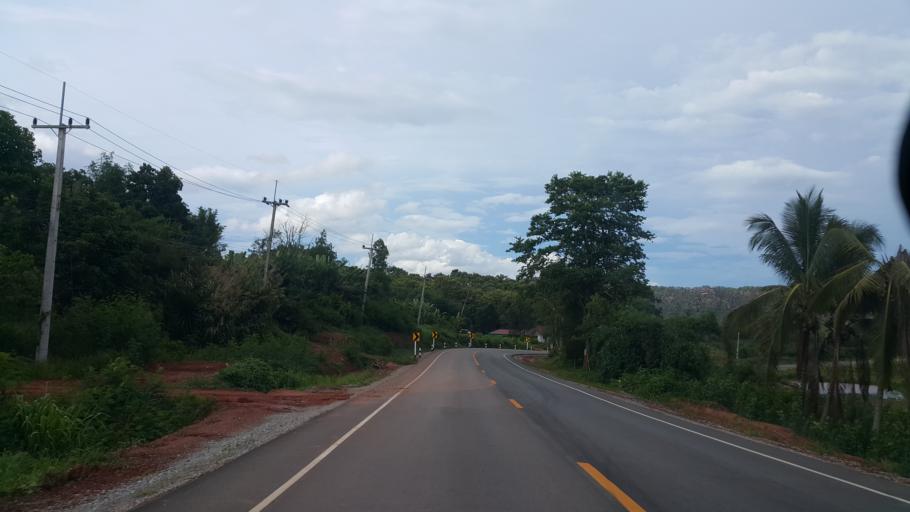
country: TH
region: Loei
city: Na Haeo
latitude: 17.5037
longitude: 101.0655
